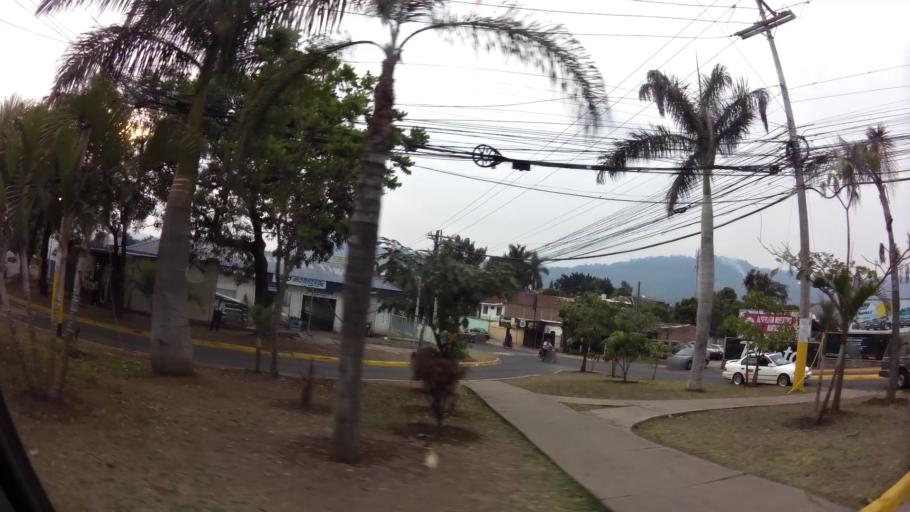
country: HN
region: Francisco Morazan
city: Tegucigalpa
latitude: 14.1007
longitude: -87.1741
